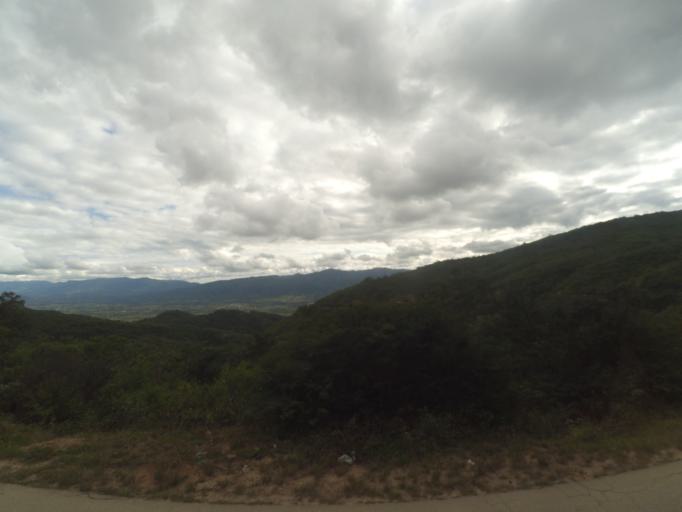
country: BO
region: Santa Cruz
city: Samaipata
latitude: -18.1769
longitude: -63.8689
